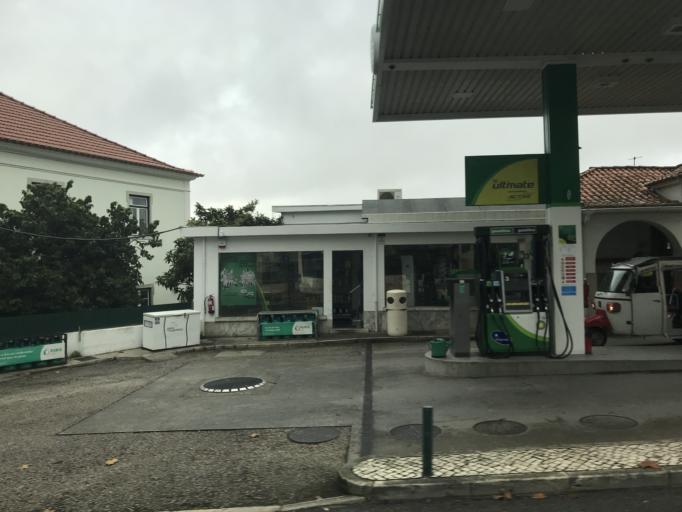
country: PT
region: Lisbon
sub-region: Sintra
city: Sintra
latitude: 38.7996
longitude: -9.3820
